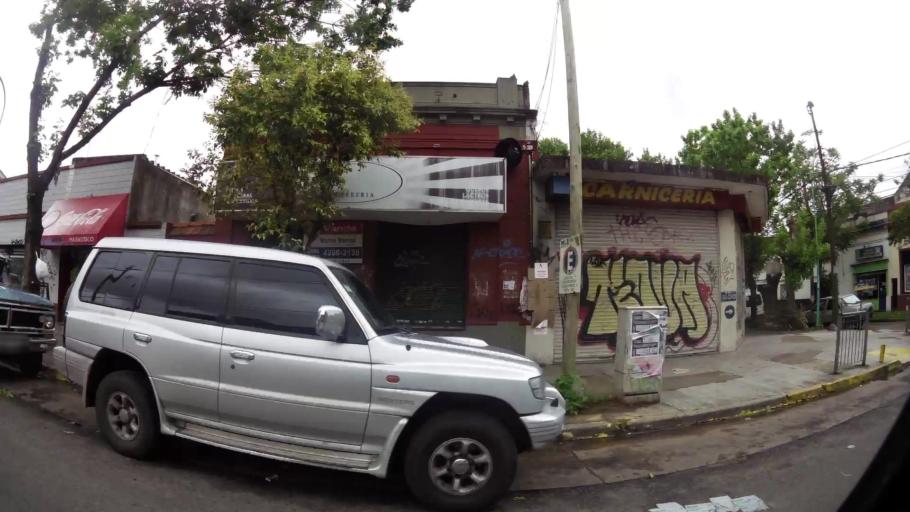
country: AR
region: Buenos Aires
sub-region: Partido de Lomas de Zamora
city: Lomas de Zamora
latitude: -34.7617
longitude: -58.3924
